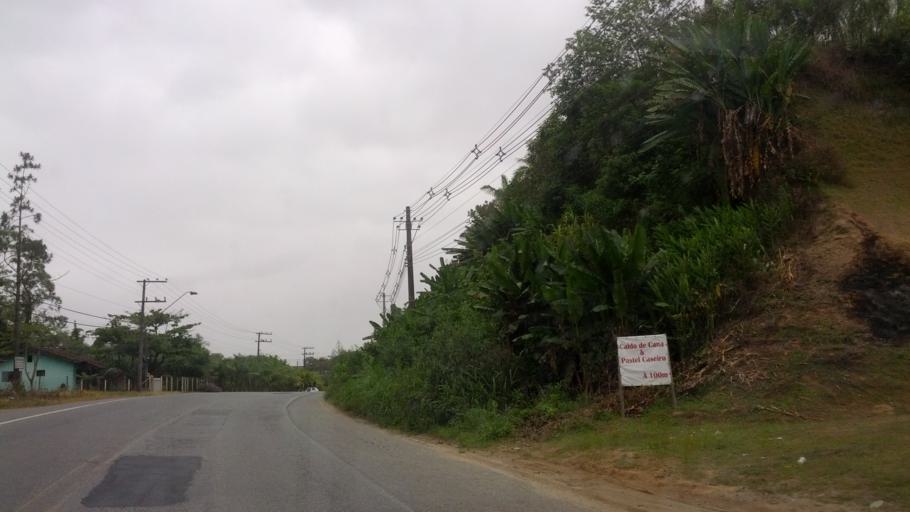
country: BR
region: Santa Catarina
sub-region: Pomerode
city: Pomerode
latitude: -26.7714
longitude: -49.0817
